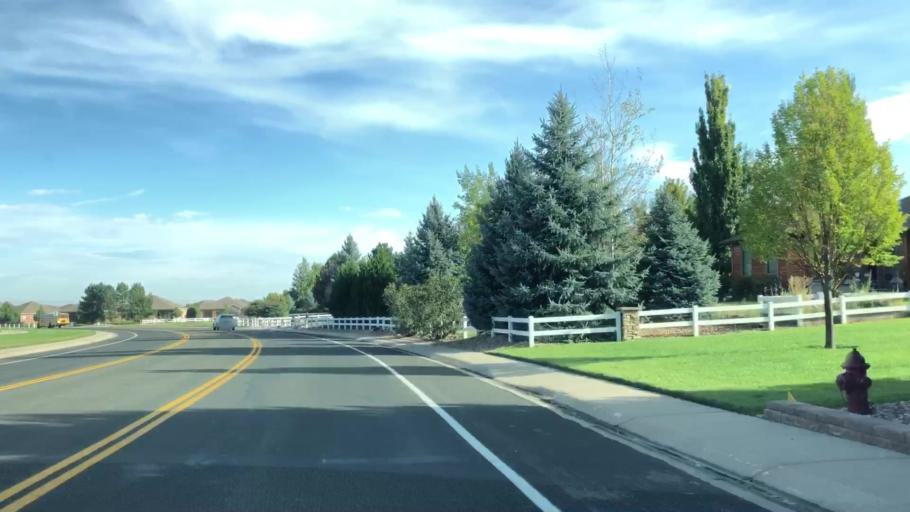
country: US
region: Colorado
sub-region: Weld County
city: Windsor
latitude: 40.4669
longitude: -104.9769
